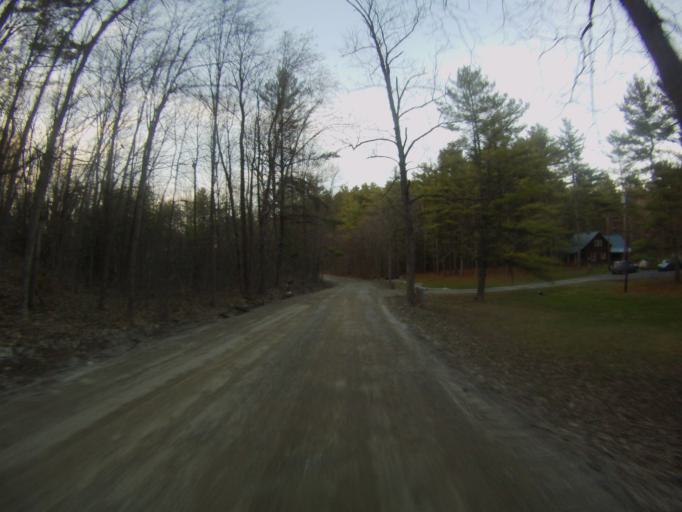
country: US
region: Vermont
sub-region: Addison County
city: Middlebury (village)
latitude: 44.0258
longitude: -73.2211
